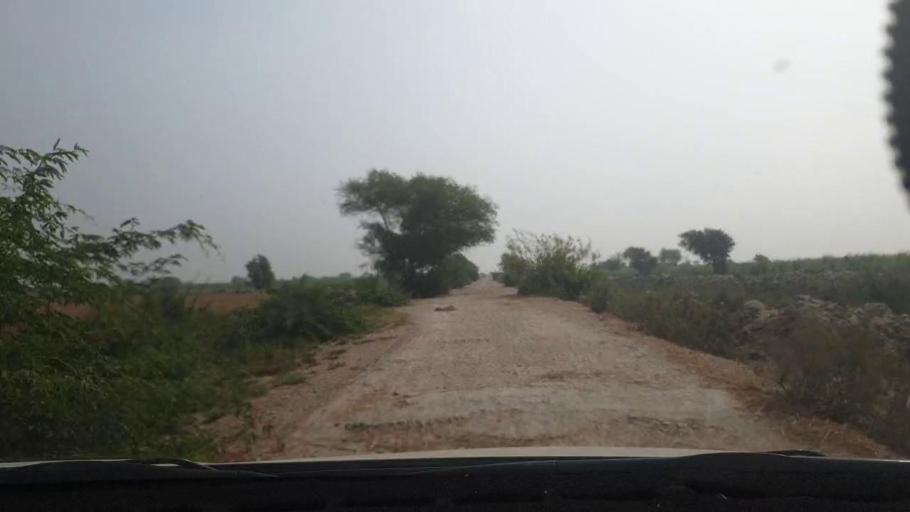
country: PK
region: Sindh
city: Tando Muhammad Khan
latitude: 25.0700
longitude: 68.5034
